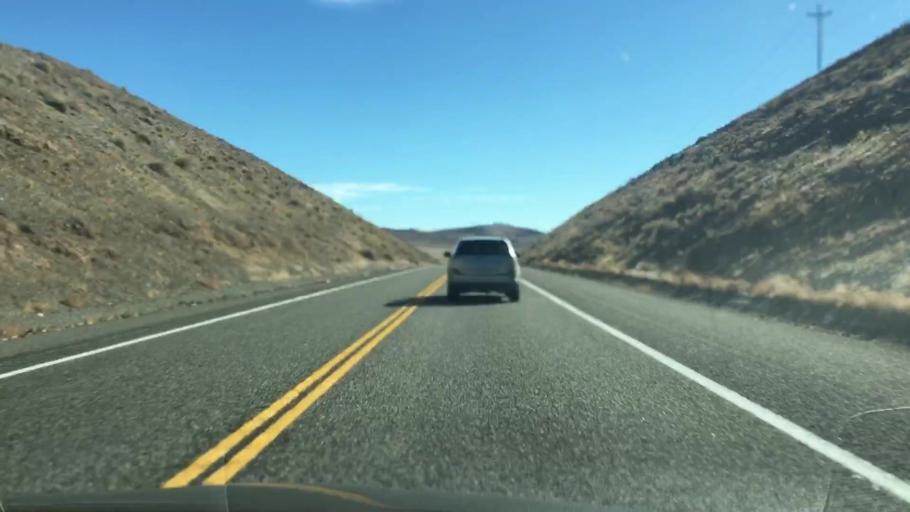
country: US
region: Nevada
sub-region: Lyon County
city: Silver Springs
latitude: 39.2144
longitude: -119.2199
